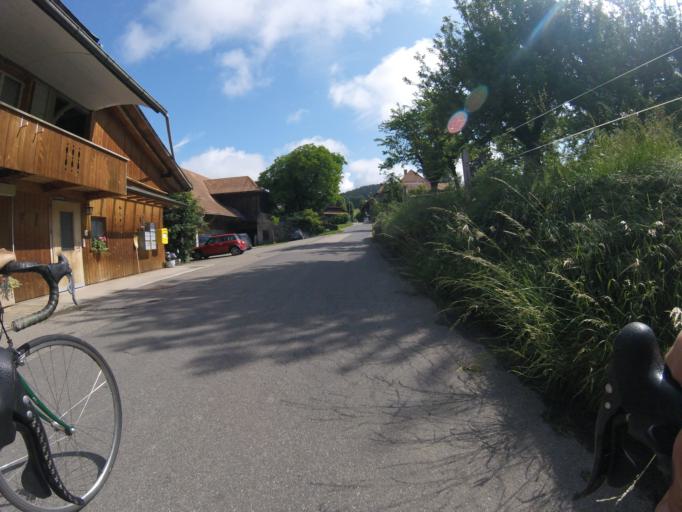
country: CH
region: Bern
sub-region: Bern-Mittelland District
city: Vechigen
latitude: 46.9415
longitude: 7.5828
